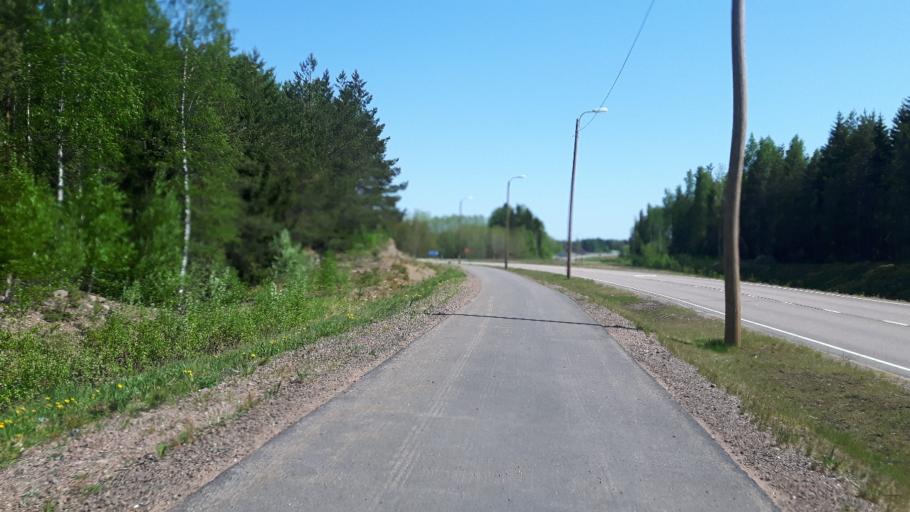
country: FI
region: Kymenlaakso
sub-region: Kotka-Hamina
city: Pyhtaeae
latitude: 60.4877
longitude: 26.5259
